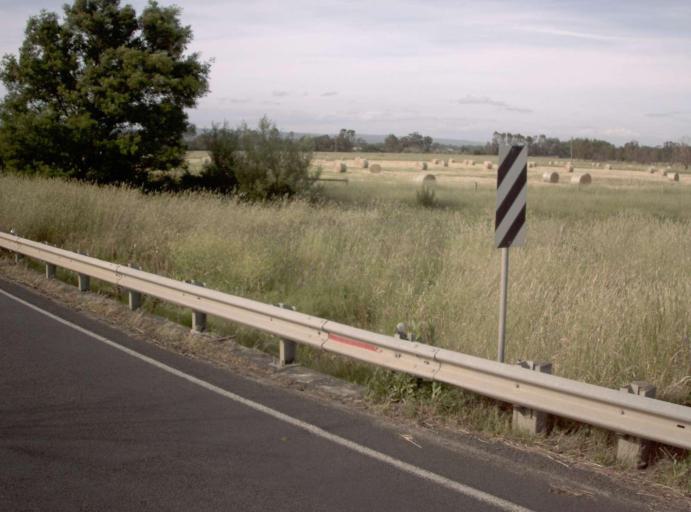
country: AU
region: Victoria
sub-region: Latrobe
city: Traralgon
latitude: -38.1601
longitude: 146.5548
